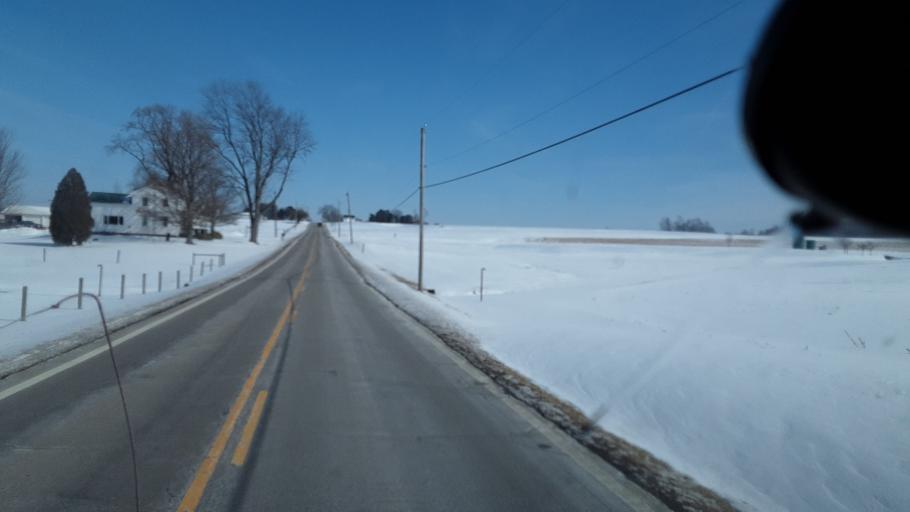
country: US
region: Ohio
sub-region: Columbiana County
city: Salem
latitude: 40.9448
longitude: -80.9299
